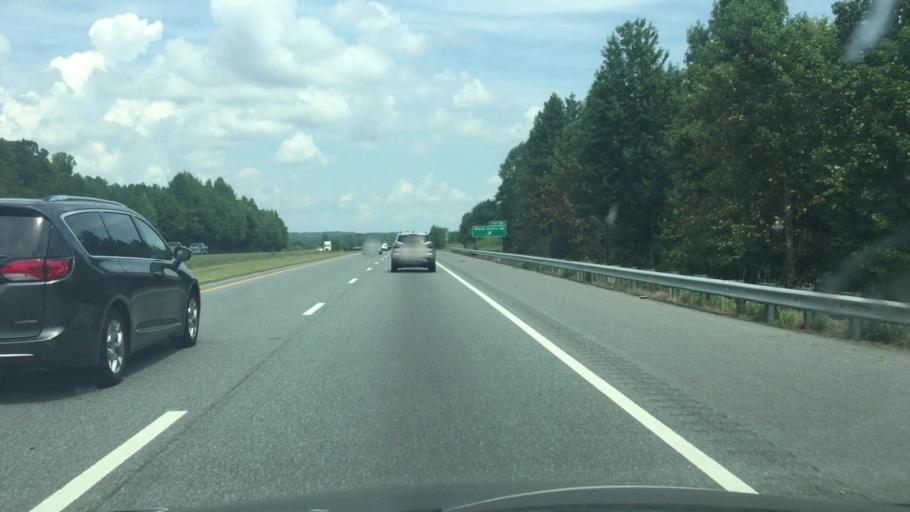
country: US
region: North Carolina
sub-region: Montgomery County
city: Biscoe
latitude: 35.4825
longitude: -79.7815
